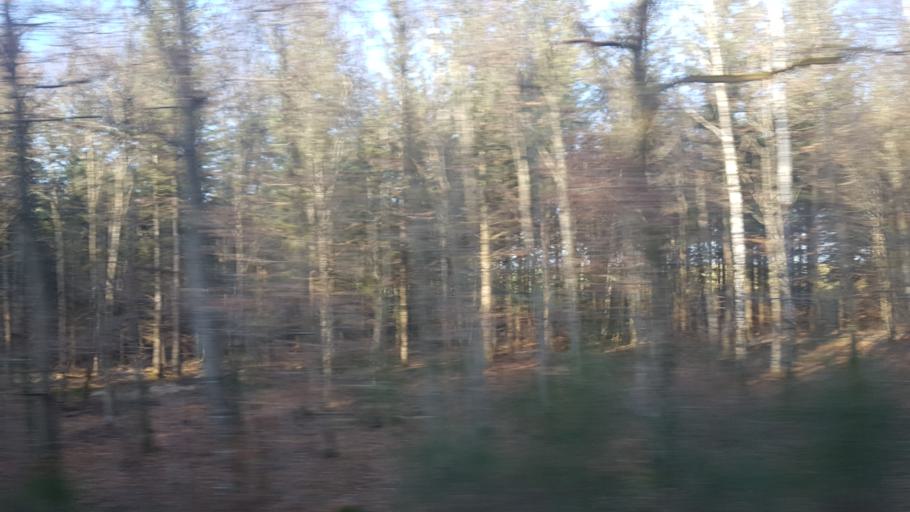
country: FR
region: Lorraine
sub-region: Departement des Vosges
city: Urimenil
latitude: 48.0868
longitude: 6.4269
